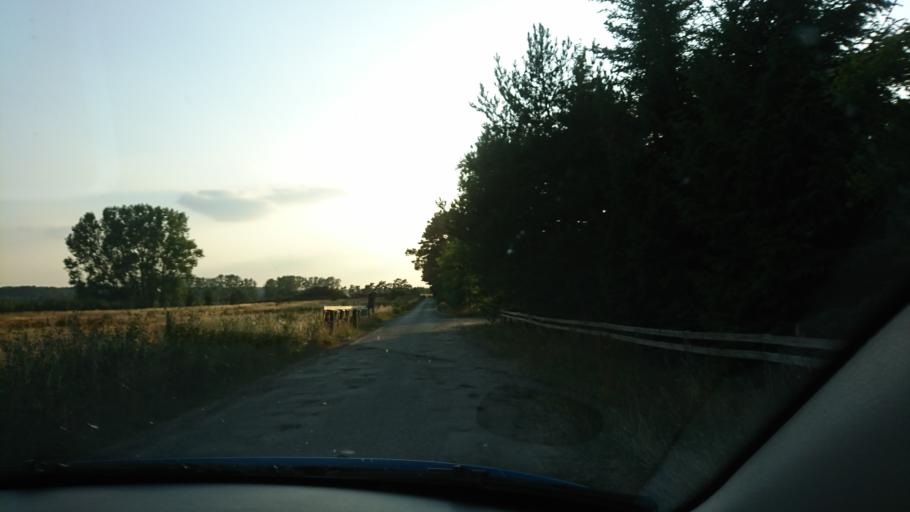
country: SE
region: Skane
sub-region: Simrishamns Kommun
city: Kivik
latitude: 55.7128
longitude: 14.1693
